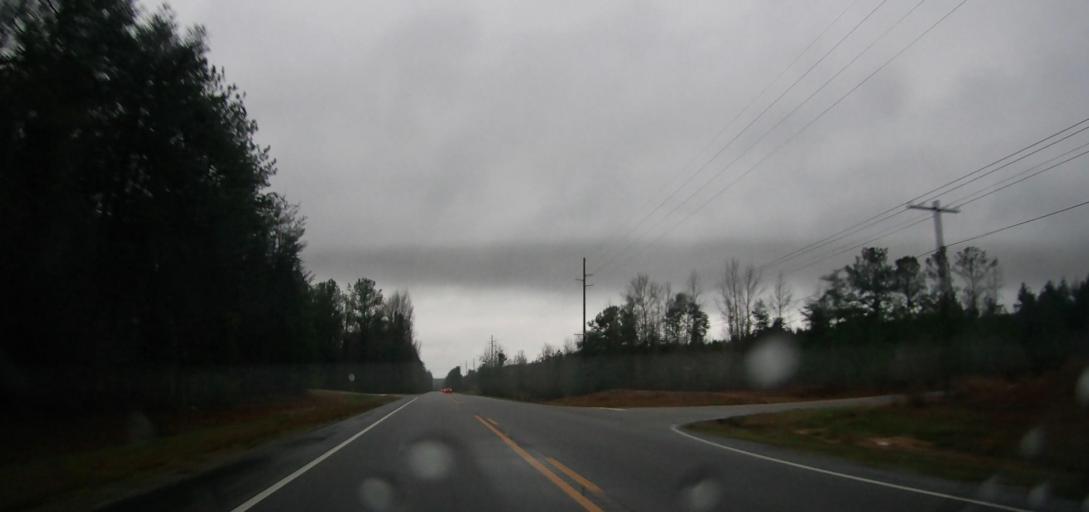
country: US
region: Alabama
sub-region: Bibb County
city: West Blocton
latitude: 33.1028
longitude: -87.1383
